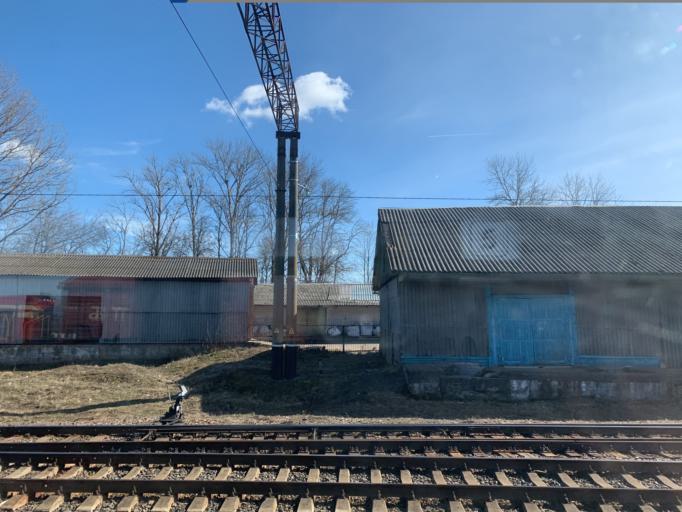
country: BY
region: Minsk
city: Haradzyeya
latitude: 53.3169
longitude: 26.5408
